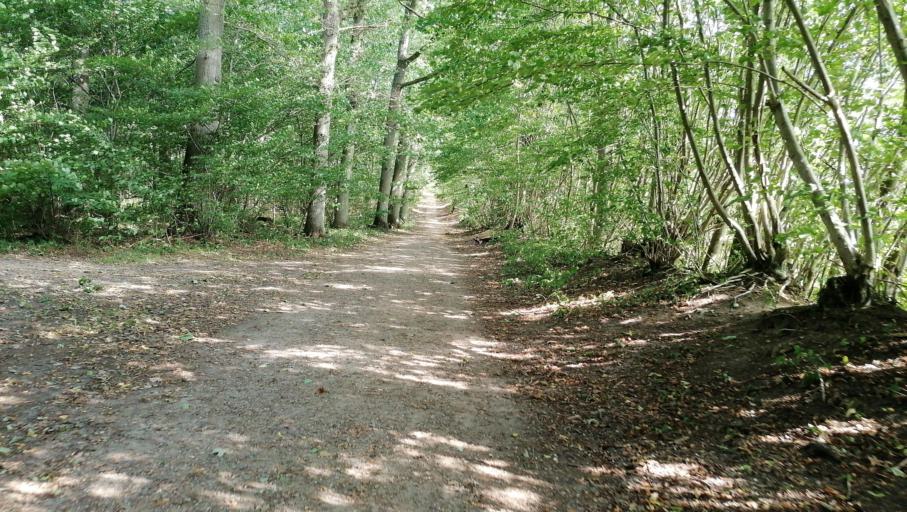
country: DK
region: Zealand
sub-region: Holbaek Kommune
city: Holbaek
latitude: 55.7091
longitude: 11.6909
